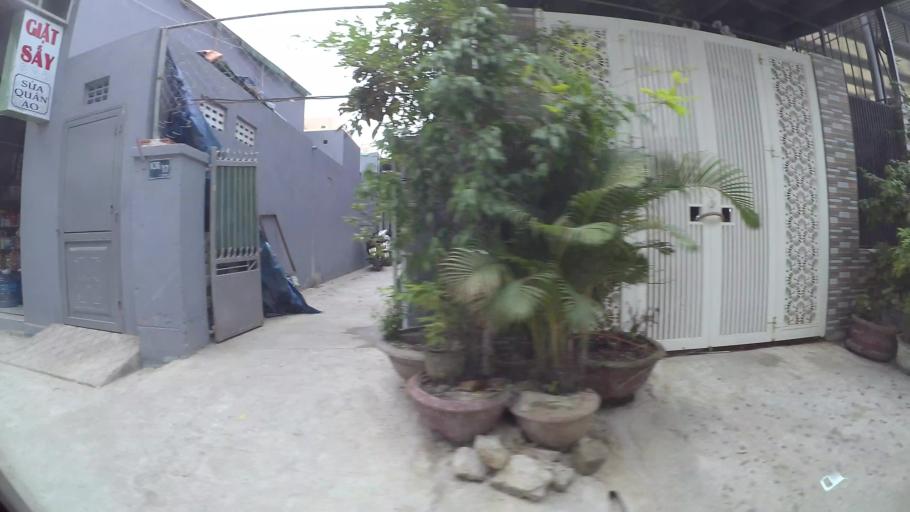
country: VN
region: Da Nang
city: Thanh Khe
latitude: 16.0756
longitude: 108.1749
